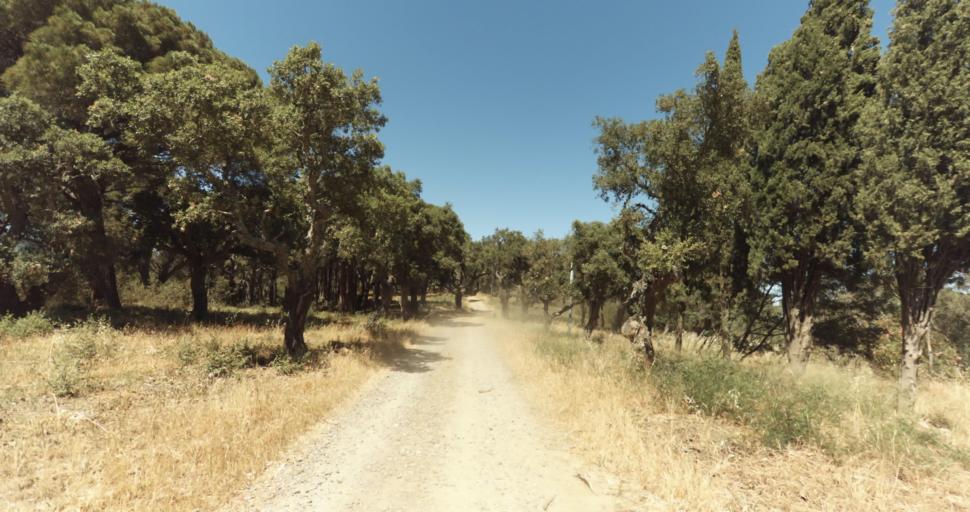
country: FR
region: Provence-Alpes-Cote d'Azur
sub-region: Departement du Var
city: Gassin
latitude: 43.2532
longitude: 6.5646
